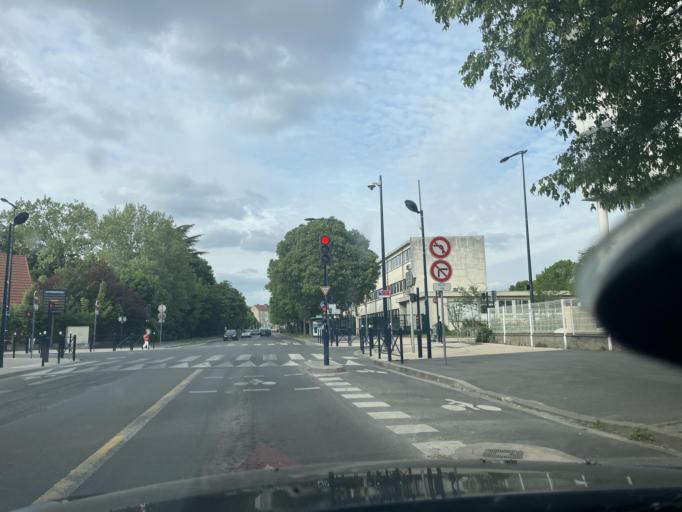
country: FR
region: Ile-de-France
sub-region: Departement de Seine-Saint-Denis
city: Dugny
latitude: 48.9492
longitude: 2.4146
